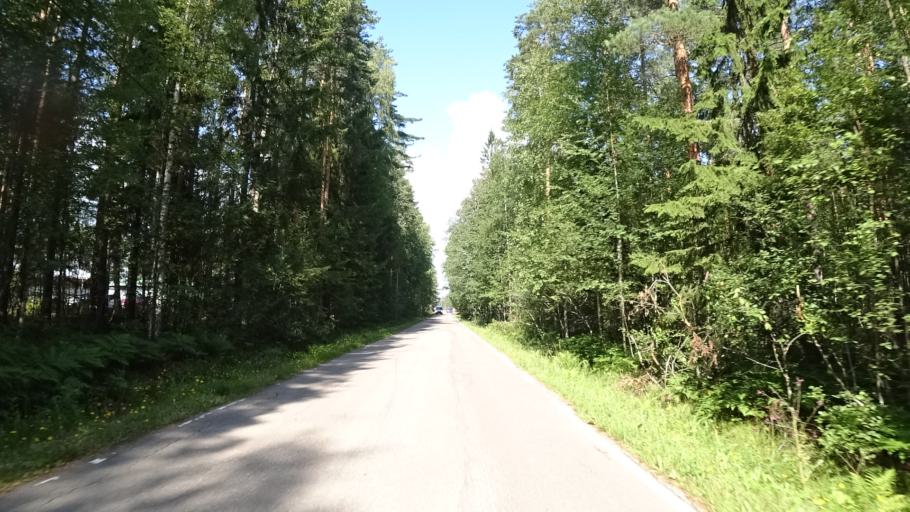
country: FI
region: Kymenlaakso
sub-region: Kotka-Hamina
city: Karhula
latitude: 60.5752
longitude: 26.8985
